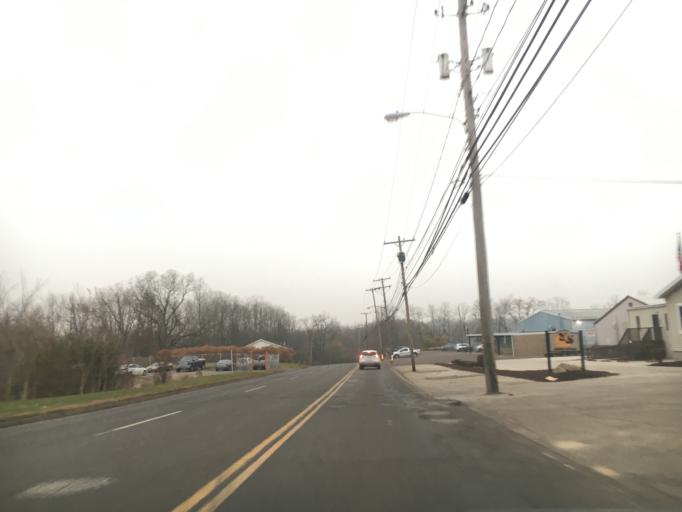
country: US
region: Ohio
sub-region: Summit County
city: Akron
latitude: 41.0908
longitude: -81.4878
